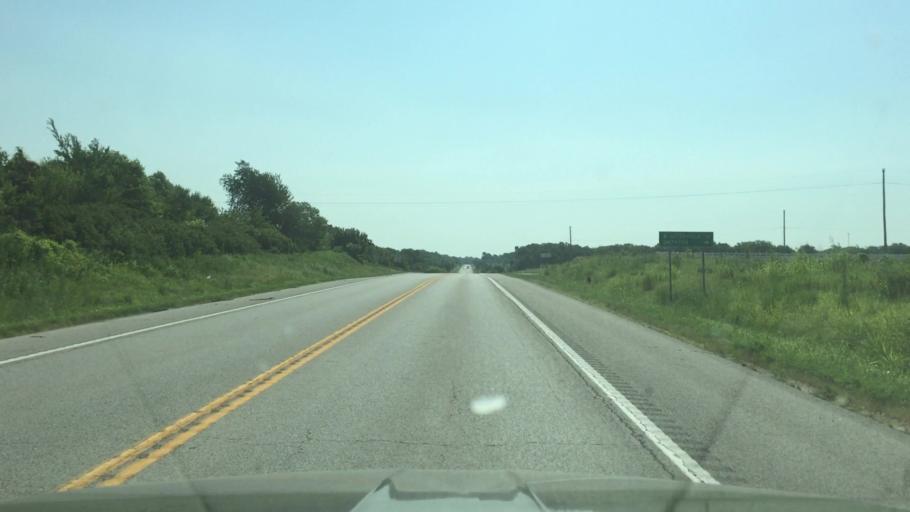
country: US
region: Missouri
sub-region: Pettis County
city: Sedalia
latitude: 38.6938
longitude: -93.0991
